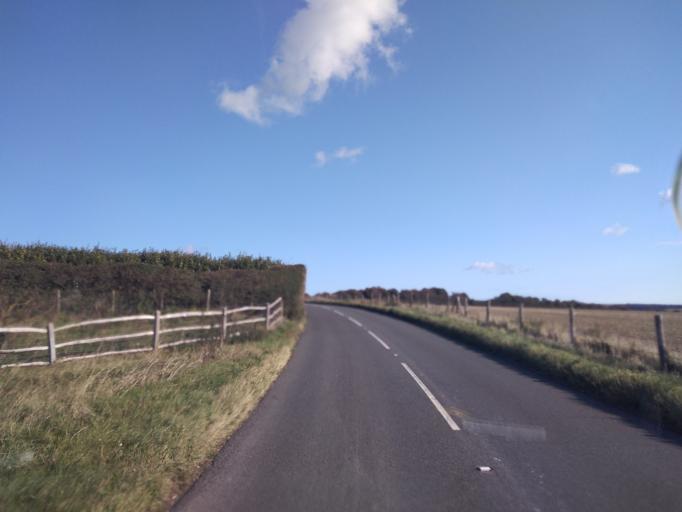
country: GB
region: England
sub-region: East Sussex
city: Seaford
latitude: 50.7883
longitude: 0.1373
